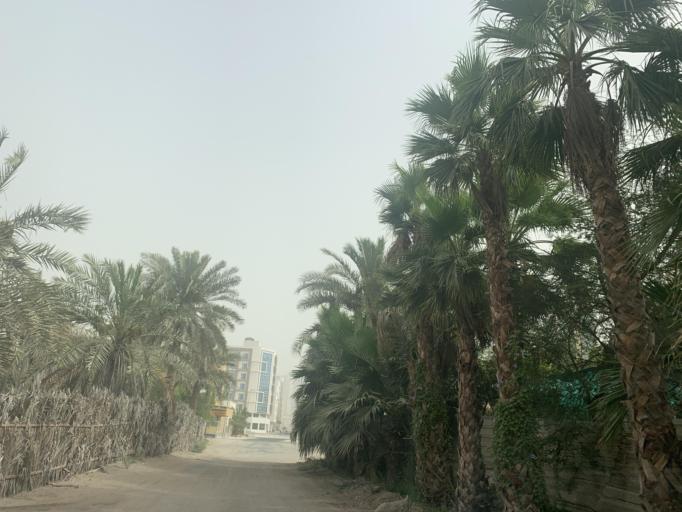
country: BH
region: Manama
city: Jidd Hafs
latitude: 26.2234
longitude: 50.5552
